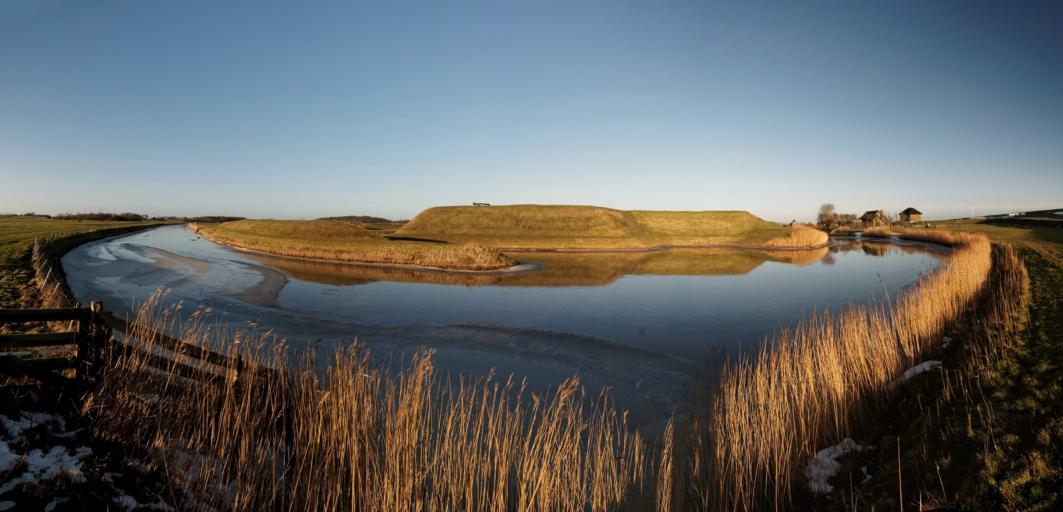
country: NL
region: North Holland
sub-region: Gemeente Texel
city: Den Burg
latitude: 53.0304
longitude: 4.8273
